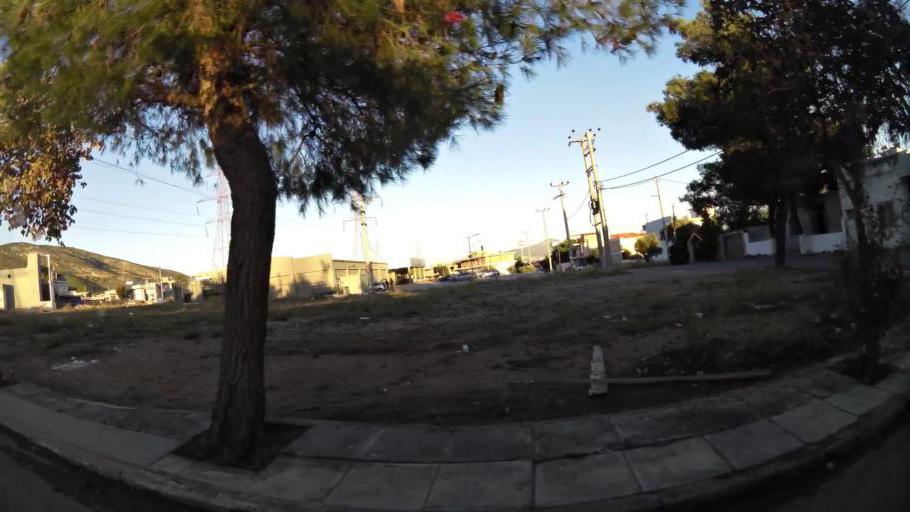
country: GR
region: Attica
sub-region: Nomarchia Dytikis Attikis
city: Ano Liosia
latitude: 38.0889
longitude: 23.6899
